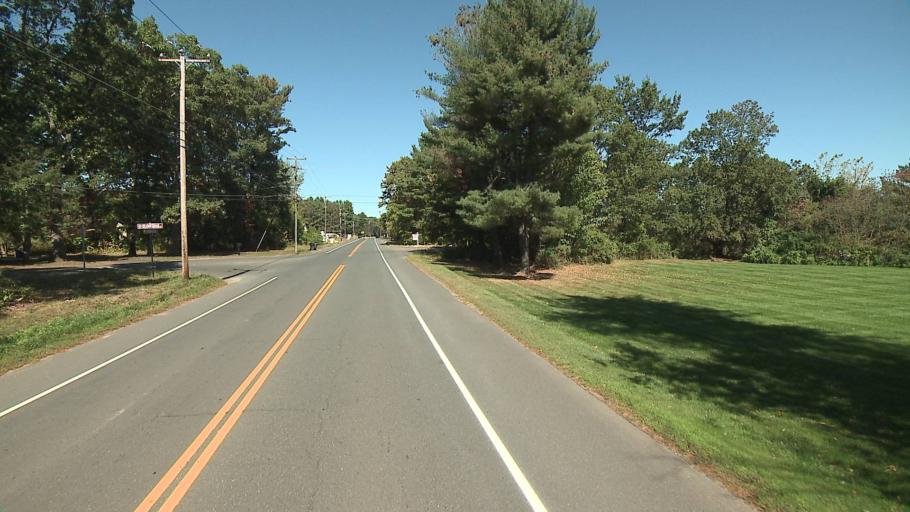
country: US
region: Connecticut
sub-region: Hartford County
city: North Granby
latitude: 41.9882
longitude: -72.8004
